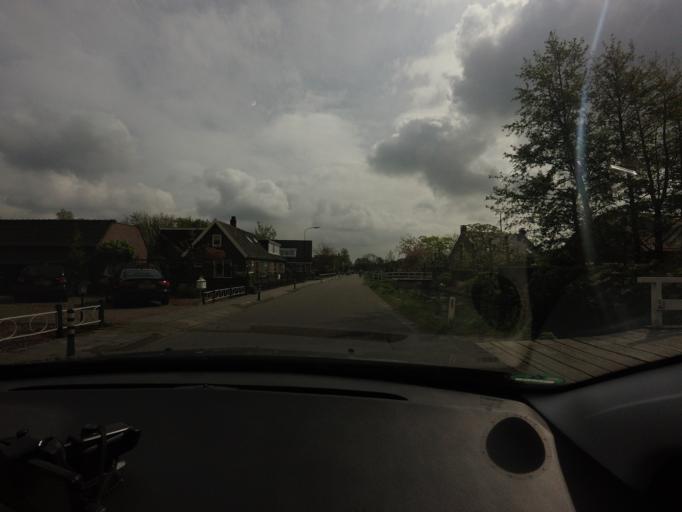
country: NL
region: Utrecht
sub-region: Gemeente De Ronde Venen
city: Mijdrecht
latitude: 52.1957
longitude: 4.9110
